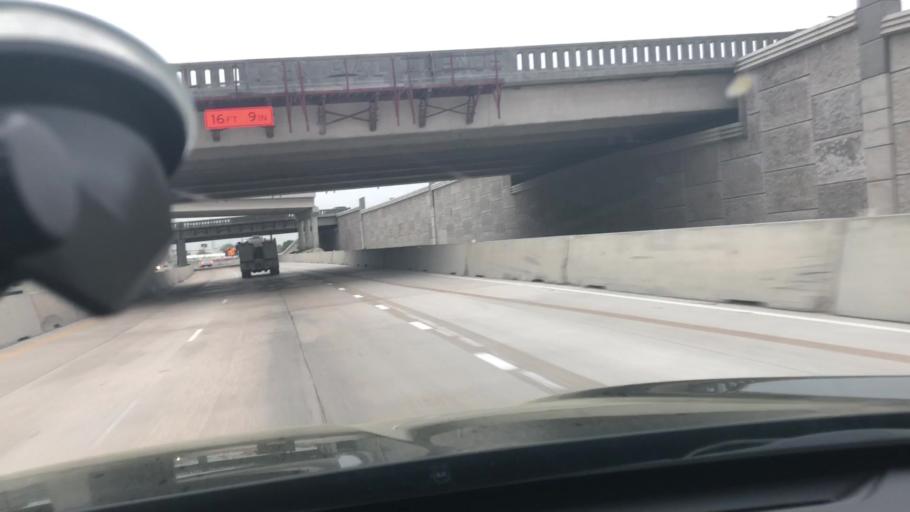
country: US
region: Texas
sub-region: Bell County
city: Temple
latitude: 31.1018
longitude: -97.3601
